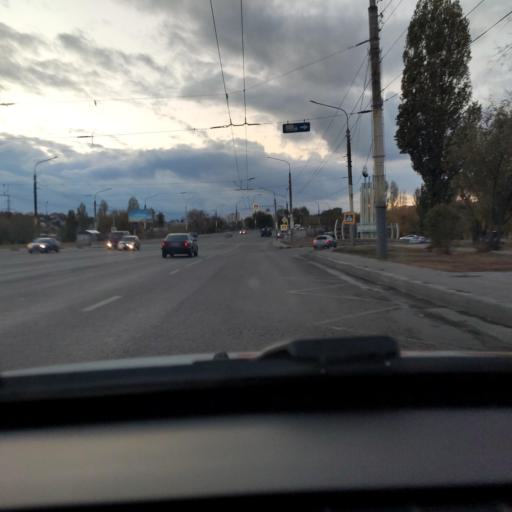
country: RU
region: Voronezj
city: Voronezh
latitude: 51.6363
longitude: 39.2117
